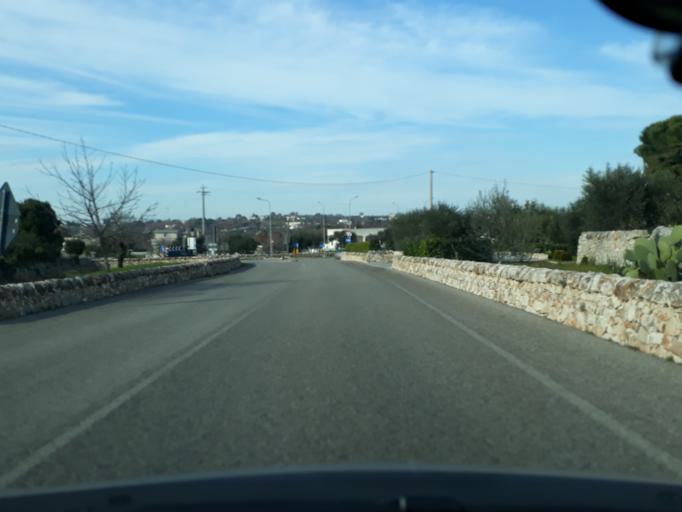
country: IT
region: Apulia
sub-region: Provincia di Bari
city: Locorotondo
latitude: 40.7627
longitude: 17.3321
